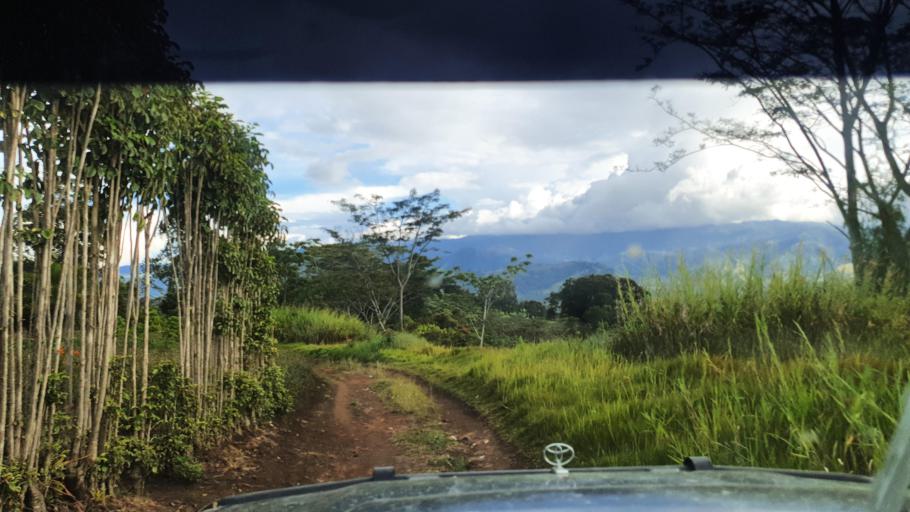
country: PG
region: Jiwaka
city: Minj
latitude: -5.9178
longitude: 144.8201
